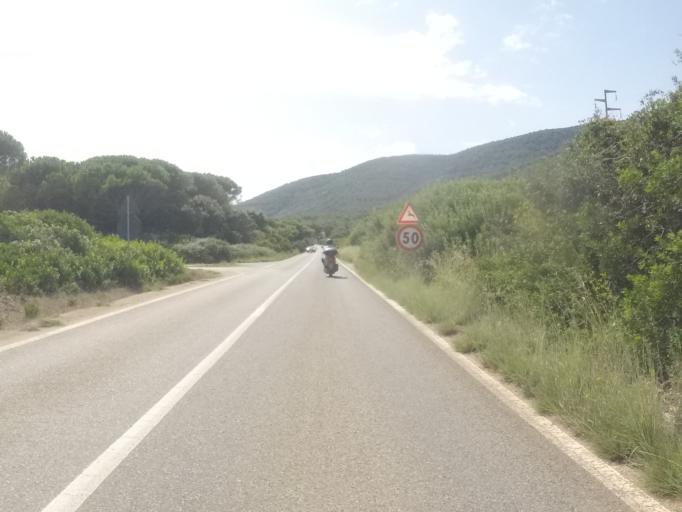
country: IT
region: Sardinia
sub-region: Provincia di Sassari
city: Alghero
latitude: 40.6190
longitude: 8.1911
